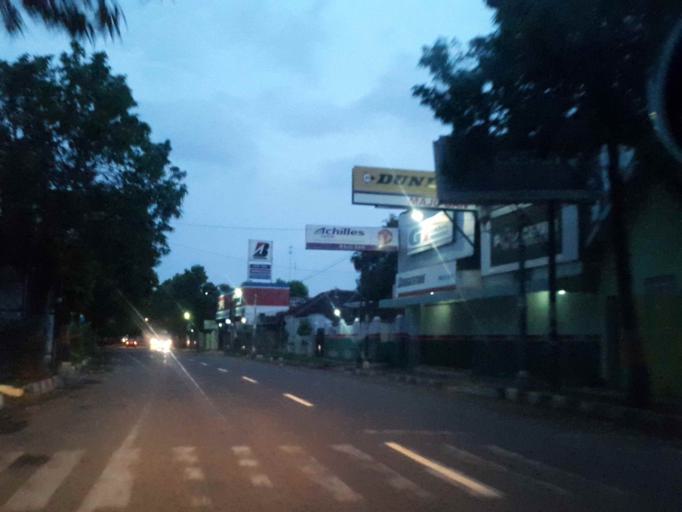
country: ID
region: Central Java
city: Pabean
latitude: -6.7045
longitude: 111.3331
